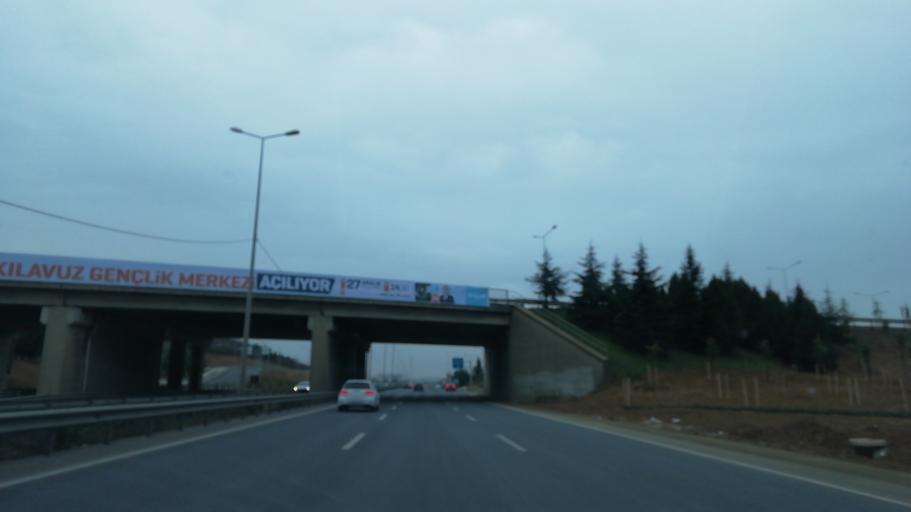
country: TR
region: Kocaeli
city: Darica
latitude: 40.8153
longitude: 29.3637
